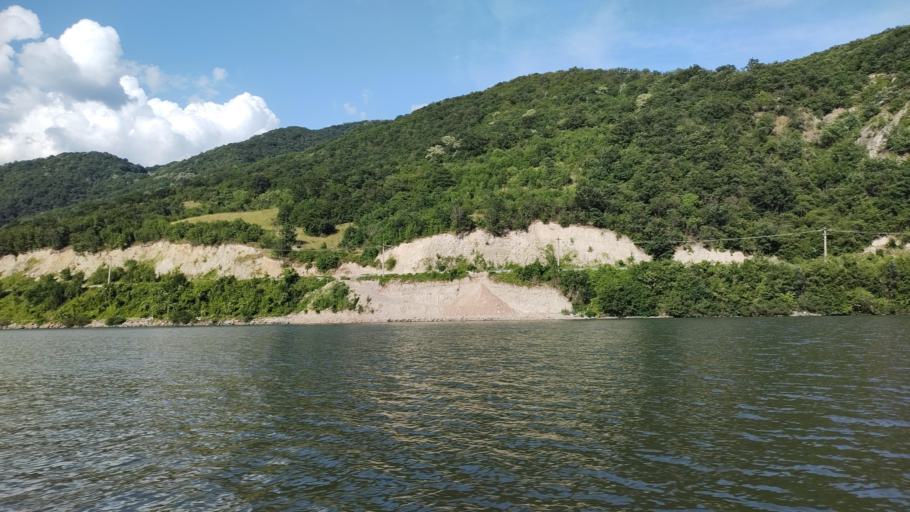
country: RO
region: Mehedinti
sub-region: Comuna Svinita
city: Svinita
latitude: 44.5666
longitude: 22.0297
